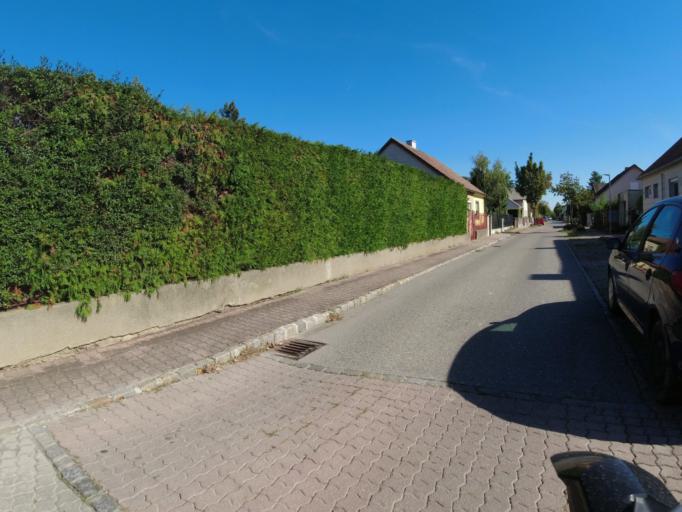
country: AT
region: Lower Austria
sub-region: Politischer Bezirk Baden
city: Traiskirchen
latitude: 48.0203
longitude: 16.3160
